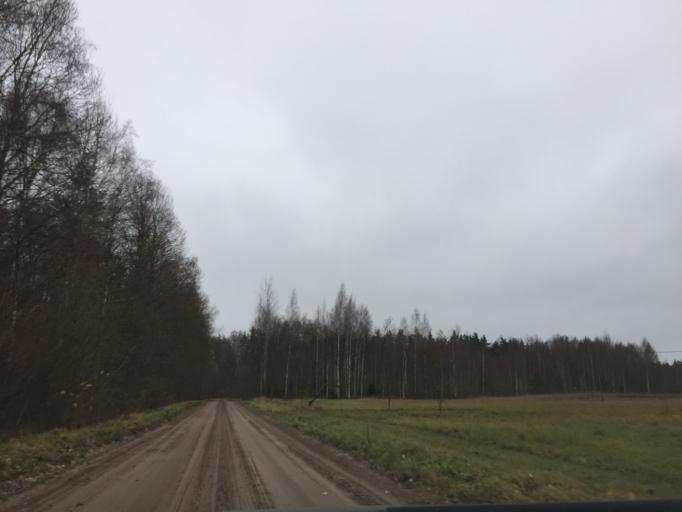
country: LV
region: Limbazu Rajons
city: Limbazi
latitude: 57.5070
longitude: 24.7597
